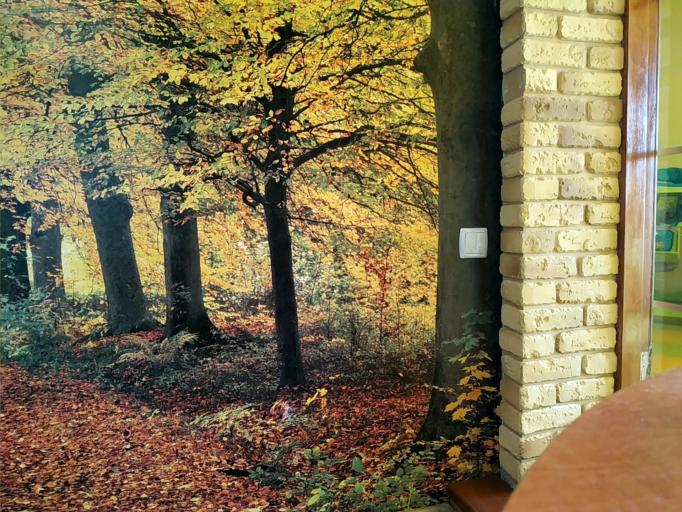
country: RU
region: Novgorod
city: Staraya Russa
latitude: 57.8329
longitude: 31.4836
